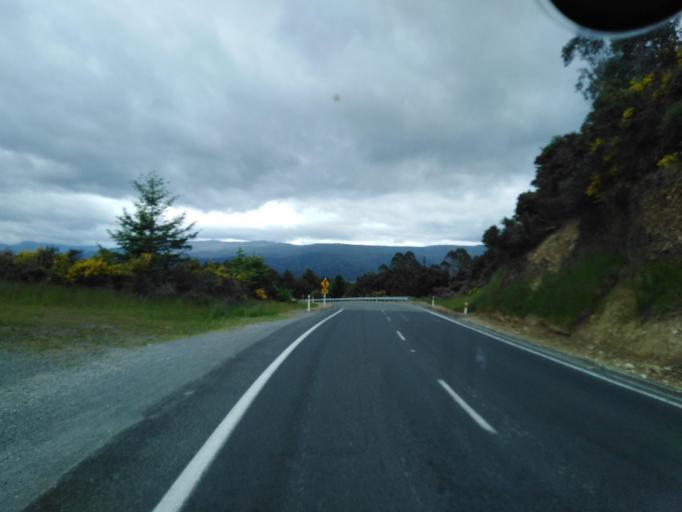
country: NZ
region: Tasman
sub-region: Tasman District
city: Wakefield
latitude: -41.6286
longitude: 172.7139
